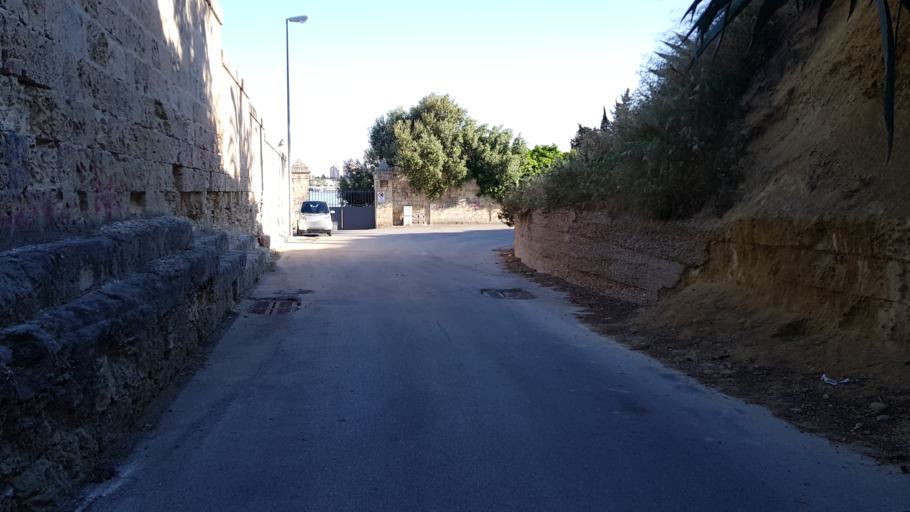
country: IT
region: Apulia
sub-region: Provincia di Brindisi
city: Materdomini
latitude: 40.6453
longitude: 17.9493
